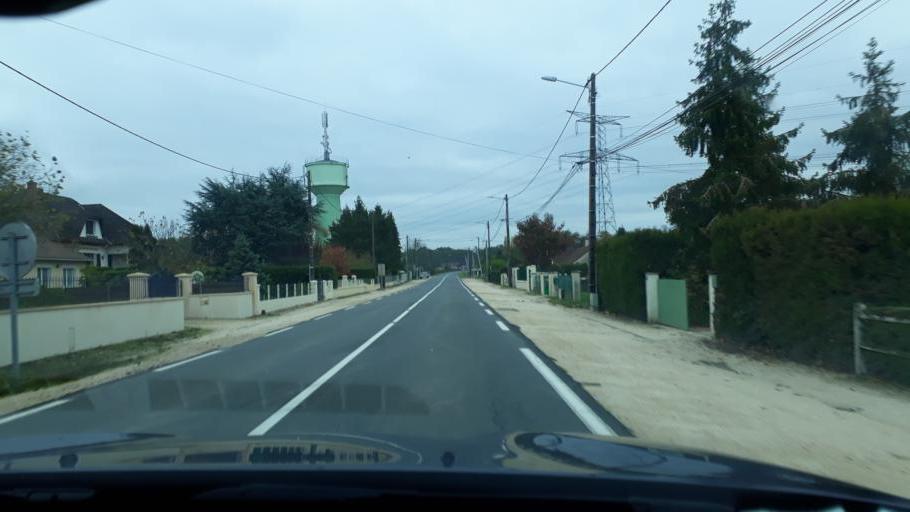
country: FR
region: Centre
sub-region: Departement du Loiret
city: Bray-en-Val
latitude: 47.8189
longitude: 2.4069
